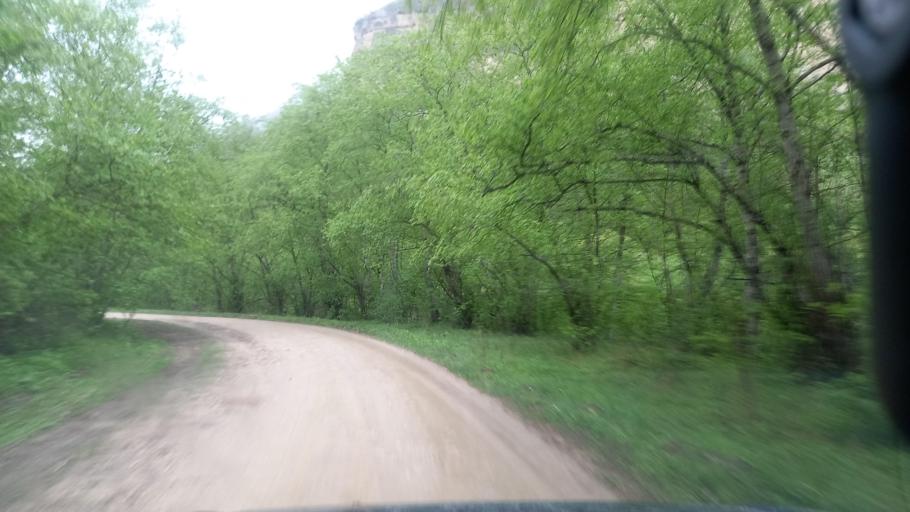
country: RU
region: Kabardino-Balkariya
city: Gundelen
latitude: 43.5801
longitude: 43.1098
